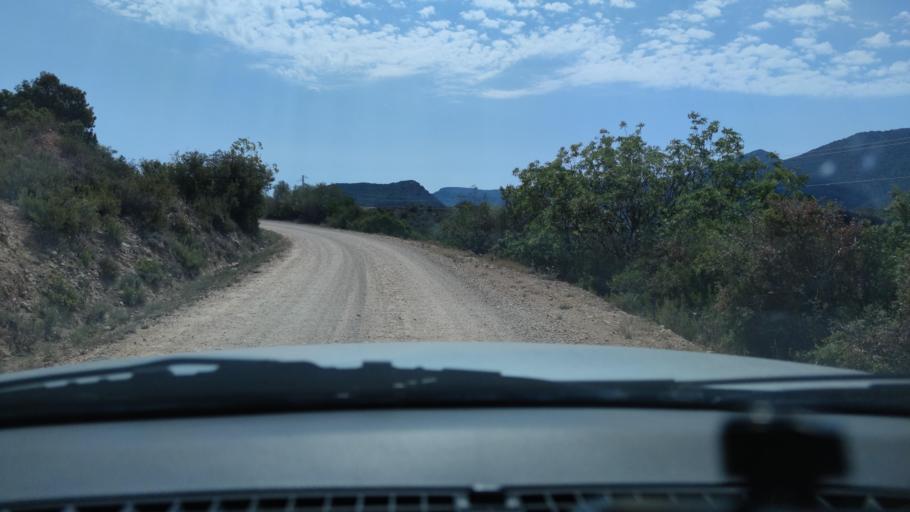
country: ES
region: Catalonia
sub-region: Provincia de Lleida
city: Camarasa
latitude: 41.9260
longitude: 0.8287
